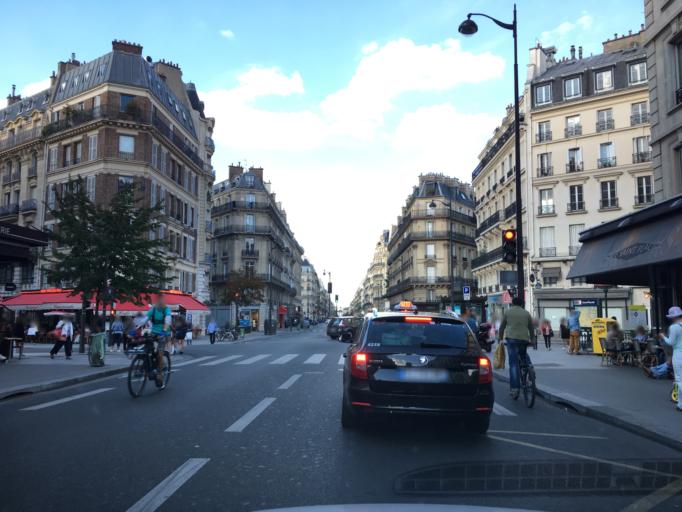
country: FR
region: Ile-de-France
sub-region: Paris
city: Paris
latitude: 48.8466
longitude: 2.3266
